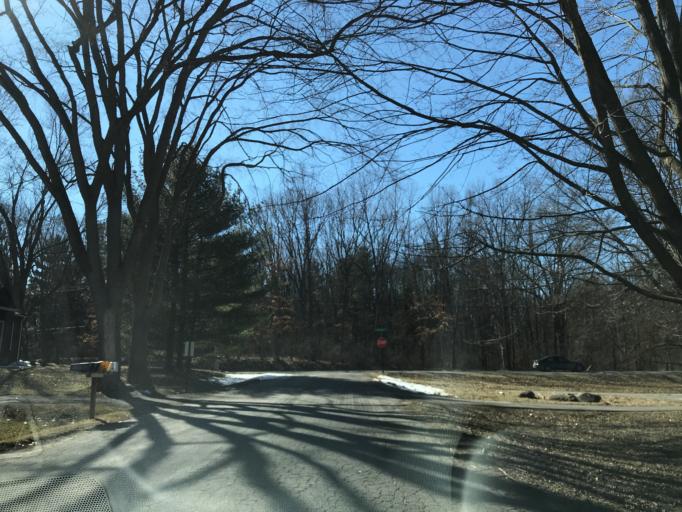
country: US
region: Michigan
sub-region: Washtenaw County
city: Ypsilanti
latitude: 42.3165
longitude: -83.6606
